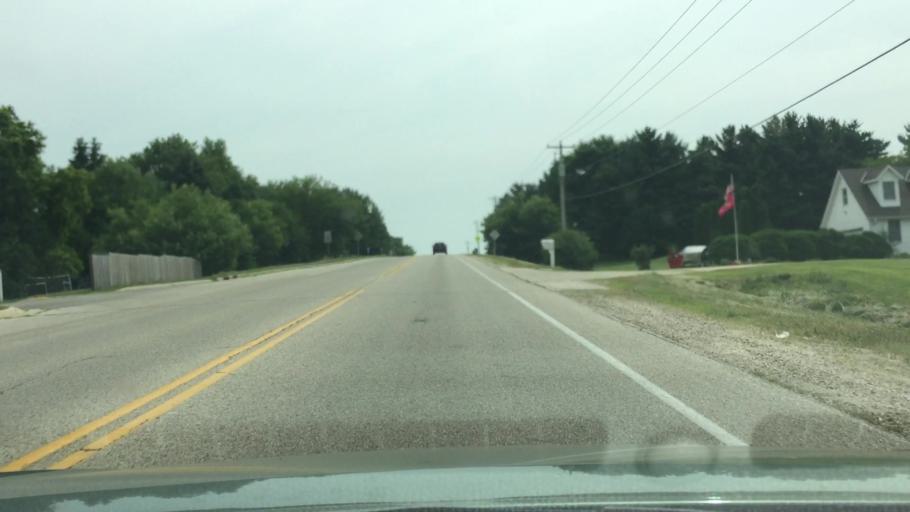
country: US
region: Wisconsin
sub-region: Waukesha County
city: Hartland
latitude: 43.0830
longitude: -88.3426
